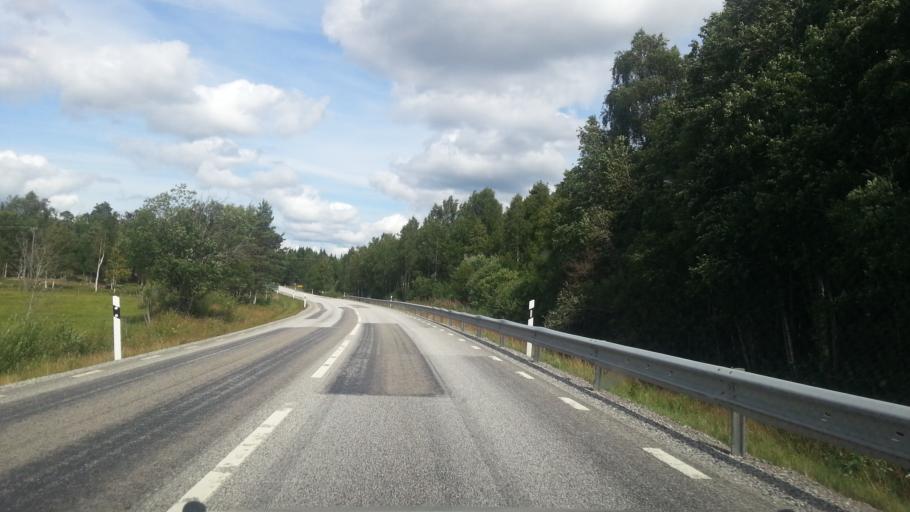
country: SE
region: Vaestmanland
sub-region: Skinnskattebergs Kommun
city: Skinnskatteberg
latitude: 59.7773
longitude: 15.5452
